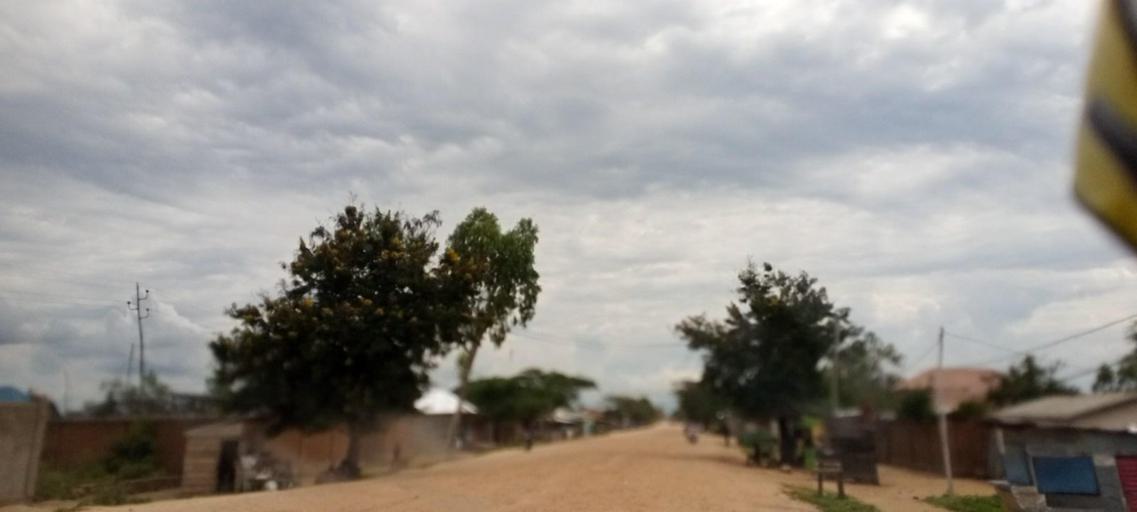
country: CD
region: South Kivu
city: Uvira
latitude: -3.3453
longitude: 29.1807
